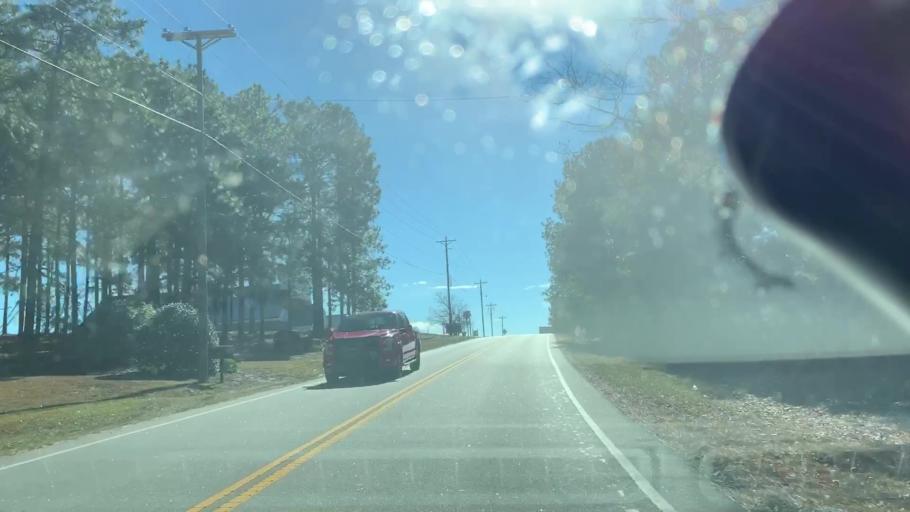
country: US
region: South Carolina
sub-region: Richland County
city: Woodfield
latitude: 34.0977
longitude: -80.8926
